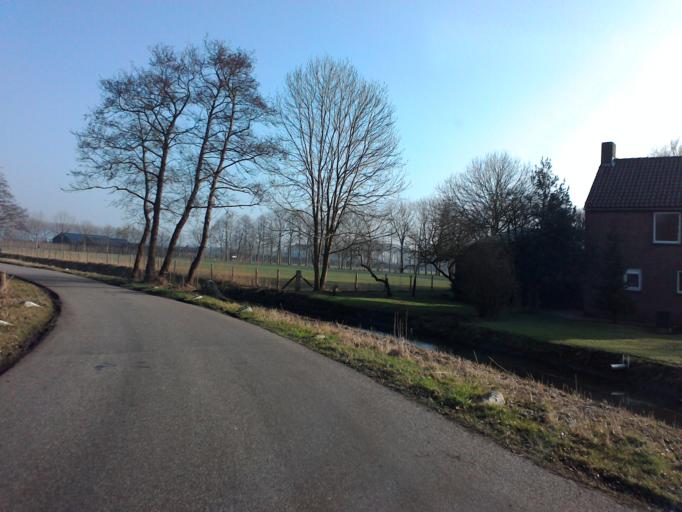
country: NL
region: Utrecht
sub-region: Gemeente Bunnik
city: Bunnik
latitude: 52.0863
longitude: 5.1899
